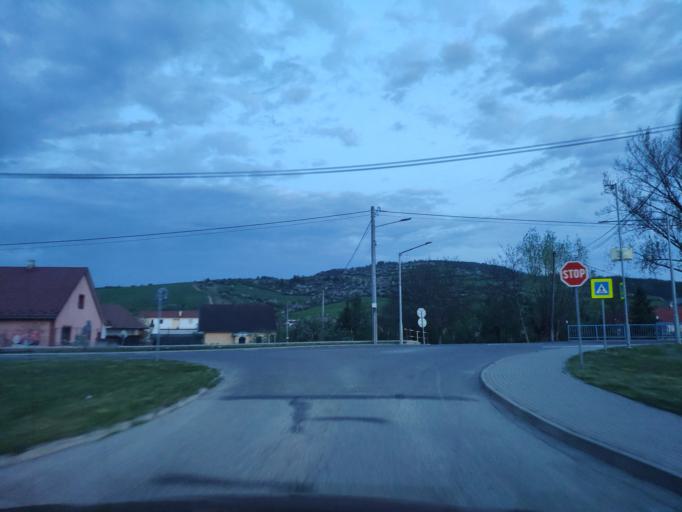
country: SK
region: Presovsky
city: Lipany
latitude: 49.1607
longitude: 20.8775
